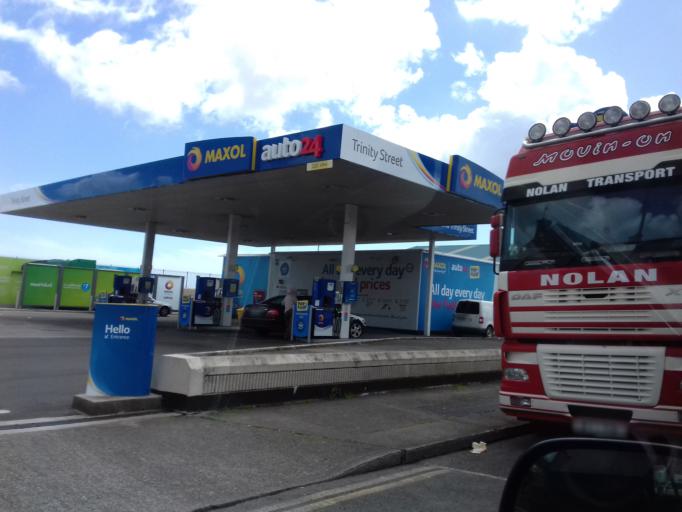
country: IE
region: Leinster
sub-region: Loch Garman
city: Loch Garman
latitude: 52.3342
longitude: -6.4552
